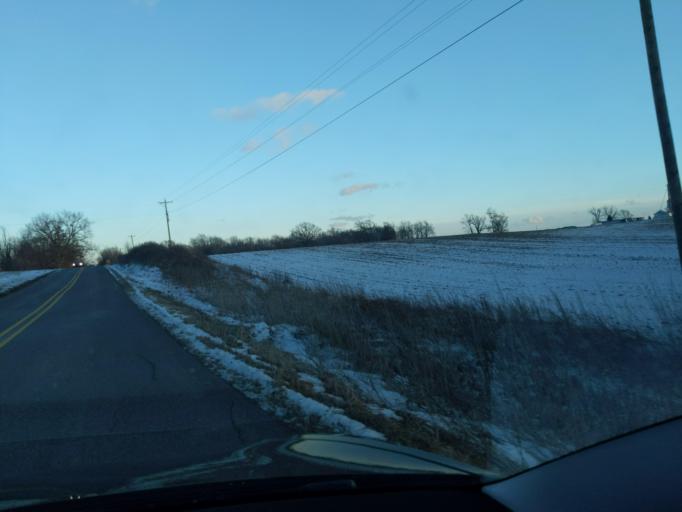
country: US
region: Michigan
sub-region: Ingham County
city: Stockbridge
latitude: 42.4540
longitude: -84.2140
